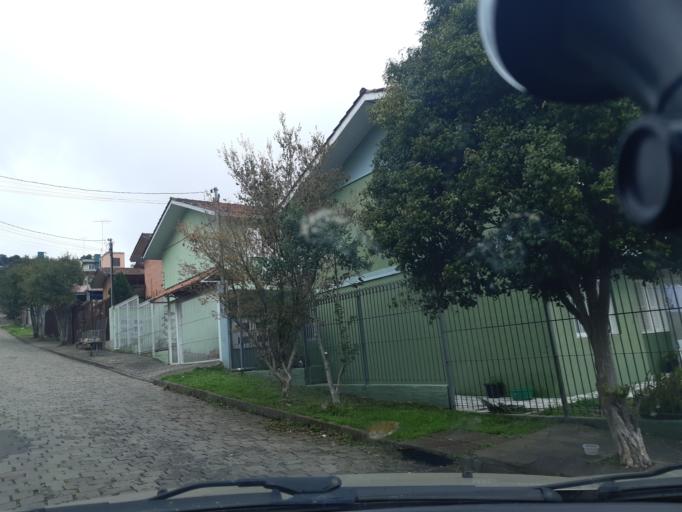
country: BR
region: Rio Grande do Sul
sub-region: Caxias Do Sul
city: Caxias do Sul
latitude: -29.1590
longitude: -51.2089
